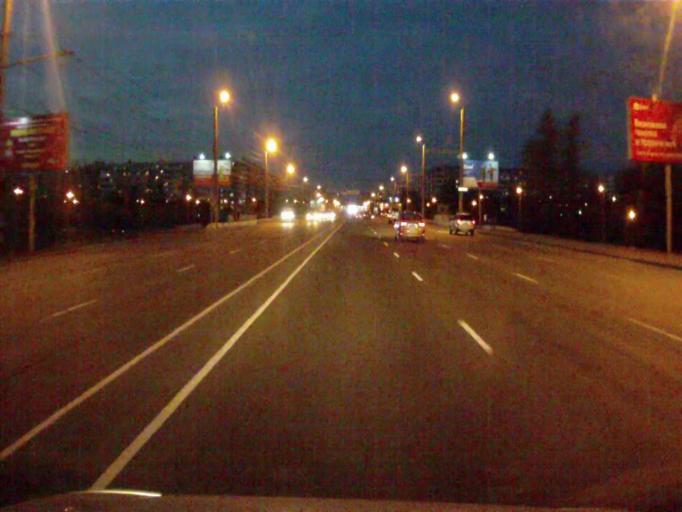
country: RU
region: Chelyabinsk
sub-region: Gorod Chelyabinsk
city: Chelyabinsk
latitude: 55.1729
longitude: 61.3582
